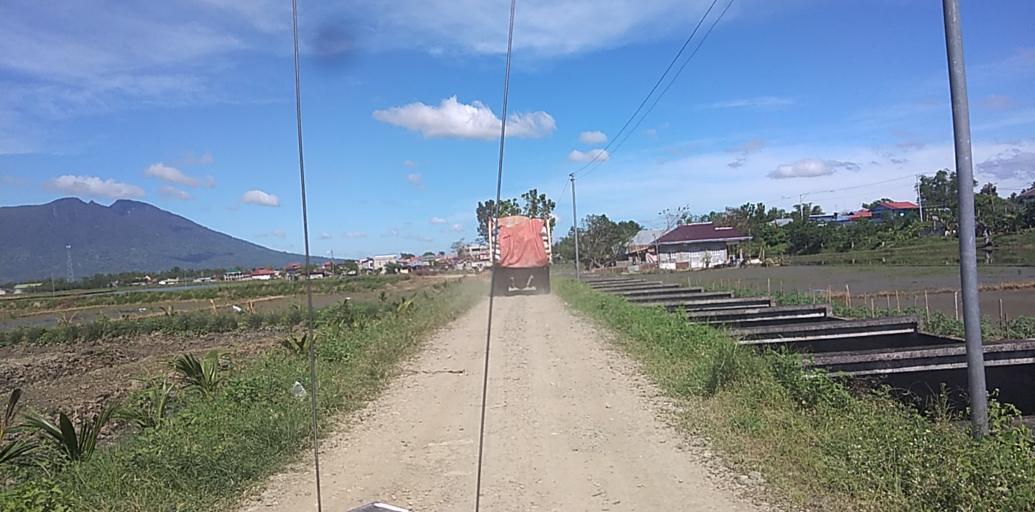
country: PH
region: Central Luzon
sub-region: Province of Pampanga
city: Candating
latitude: 15.1290
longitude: 120.8078
